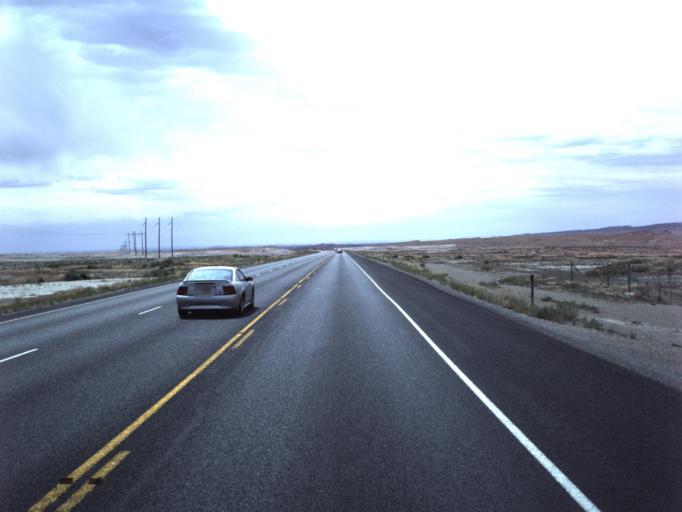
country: US
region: Utah
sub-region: Carbon County
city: East Carbon City
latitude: 39.1615
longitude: -110.3382
